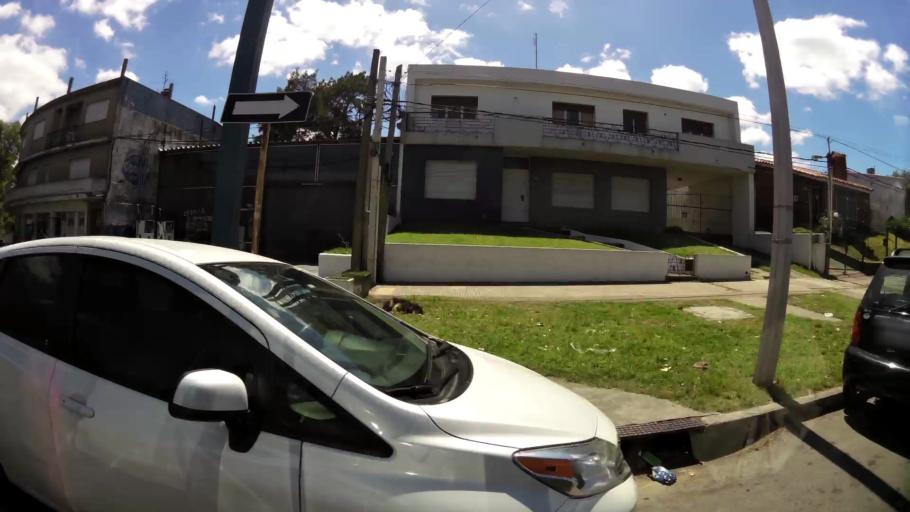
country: UY
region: Montevideo
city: Montevideo
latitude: -34.8624
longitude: -56.1512
